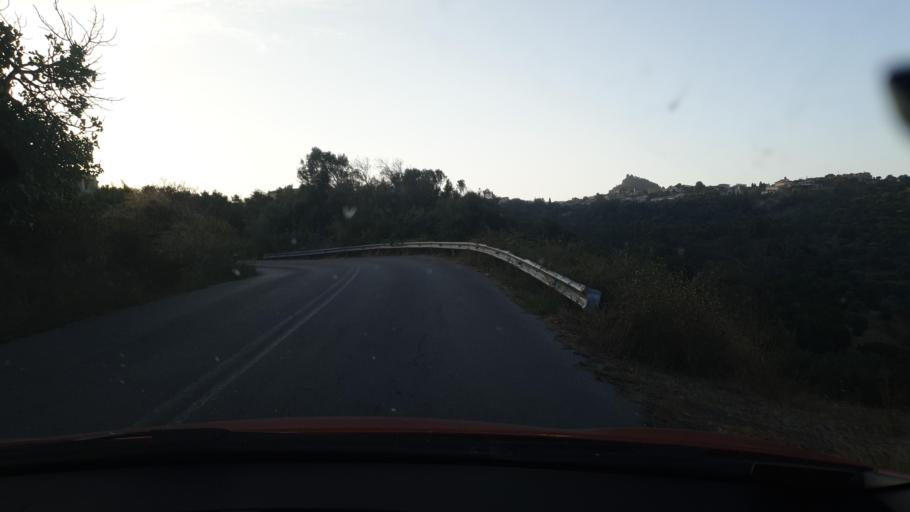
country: GR
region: Central Greece
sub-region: Nomos Evvoias
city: Oxilithos
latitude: 38.5730
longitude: 24.1195
